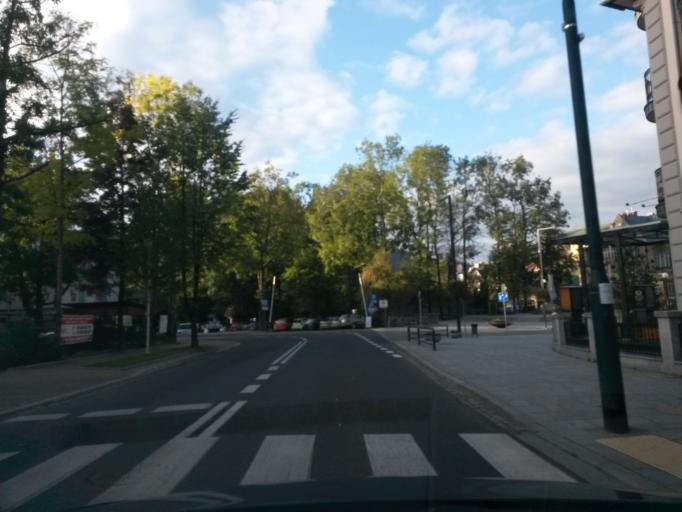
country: PL
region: Lesser Poland Voivodeship
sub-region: Powiat tatrzanski
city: Zakopane
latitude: 49.2924
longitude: 19.9535
